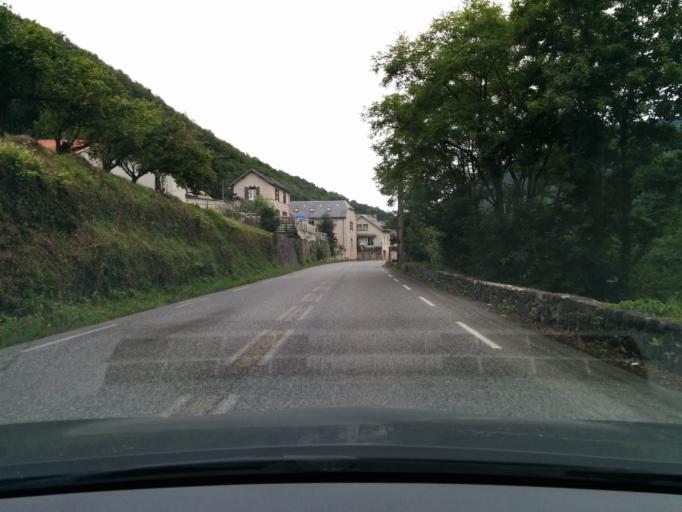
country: FR
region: Midi-Pyrenees
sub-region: Departement des Hautes-Pyrenees
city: La Barthe-de-Neste
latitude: 42.9960
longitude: 0.3727
